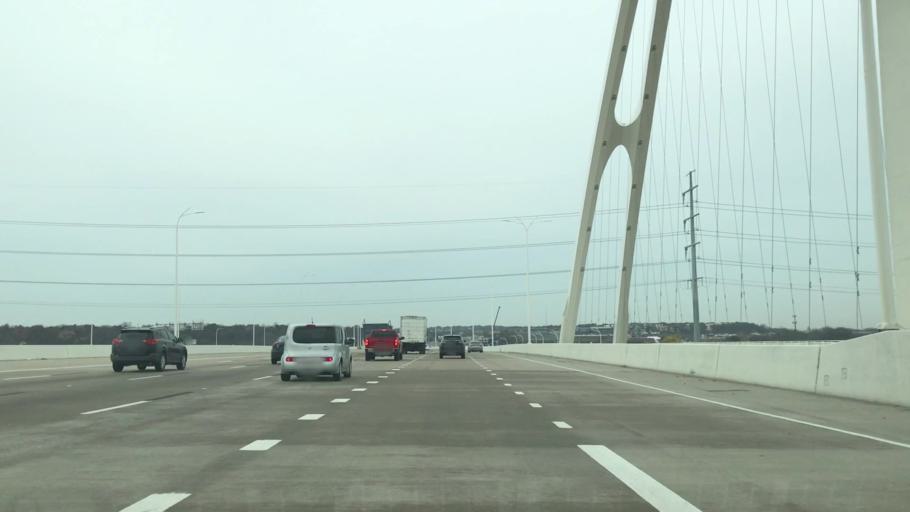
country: US
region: Texas
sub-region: Dallas County
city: Dallas
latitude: 32.7705
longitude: -96.8182
